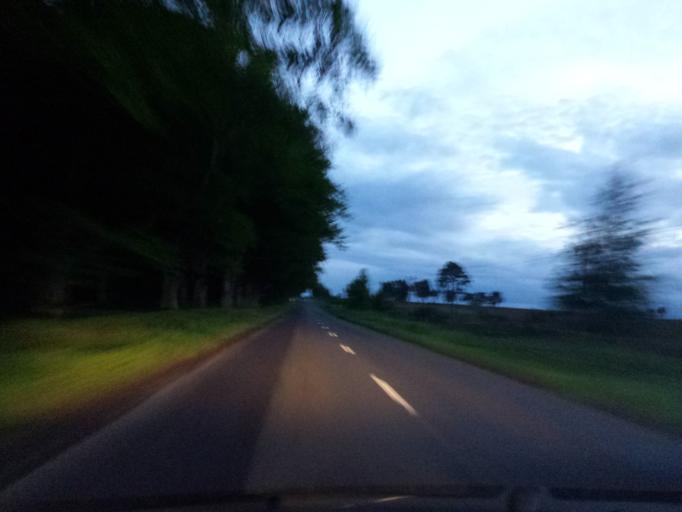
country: GB
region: Scotland
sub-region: The Scottish Borders
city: Duns
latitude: 55.7350
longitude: -2.4333
